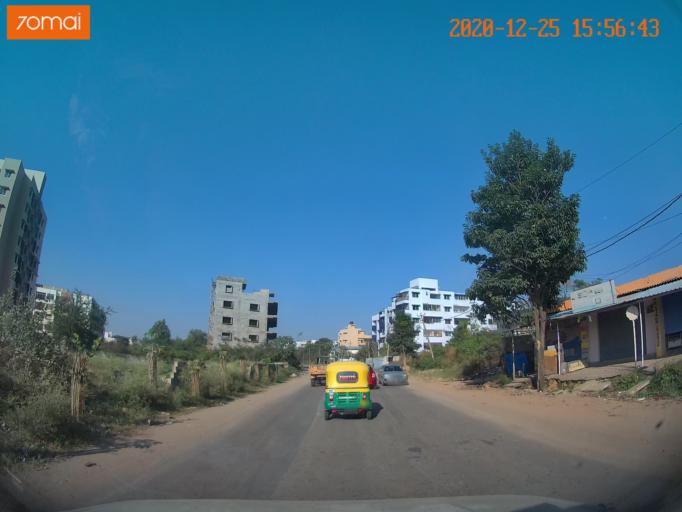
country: IN
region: Karnataka
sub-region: Bangalore Urban
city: Bangalore
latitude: 12.8664
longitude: 77.6201
